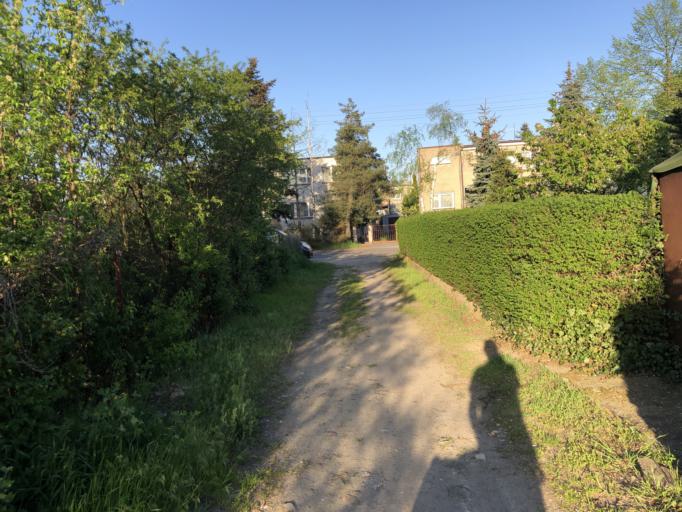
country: PL
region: Greater Poland Voivodeship
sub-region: Powiat poznanski
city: Lubon
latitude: 52.3658
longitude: 16.8832
